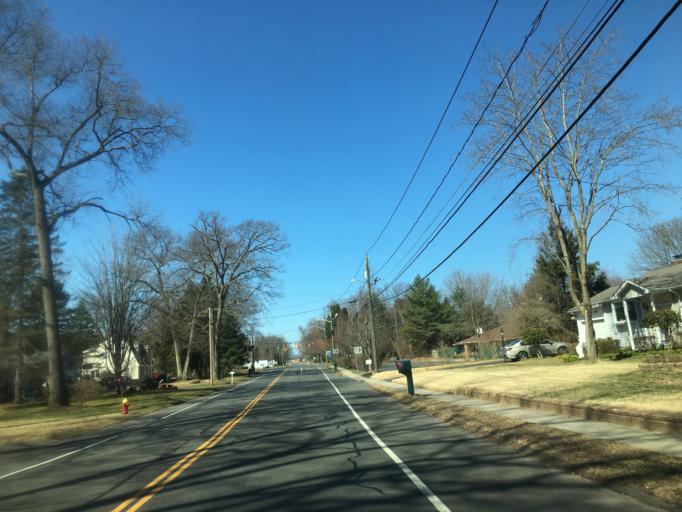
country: US
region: Connecticut
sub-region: Hartford County
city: South Windsor
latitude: 41.8083
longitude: -72.6003
